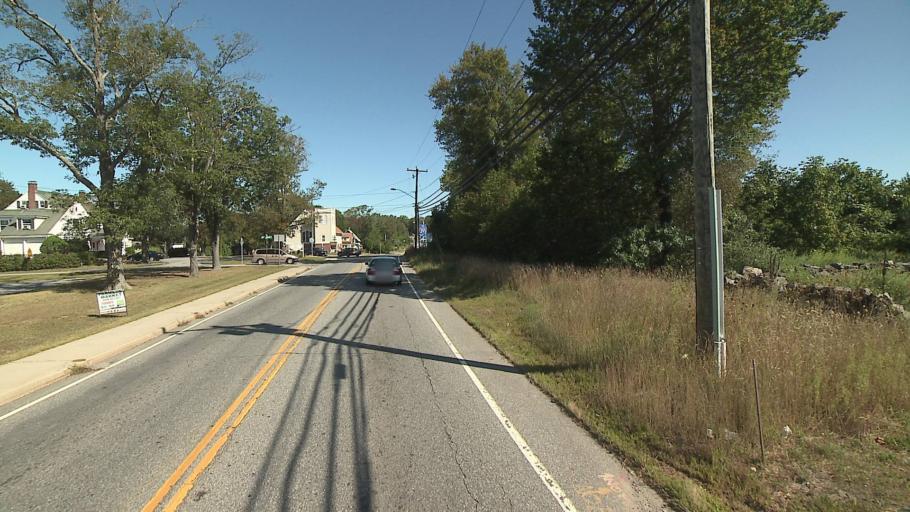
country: US
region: Connecticut
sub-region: Windham County
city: Plainfield
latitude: 41.6762
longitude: -71.9154
